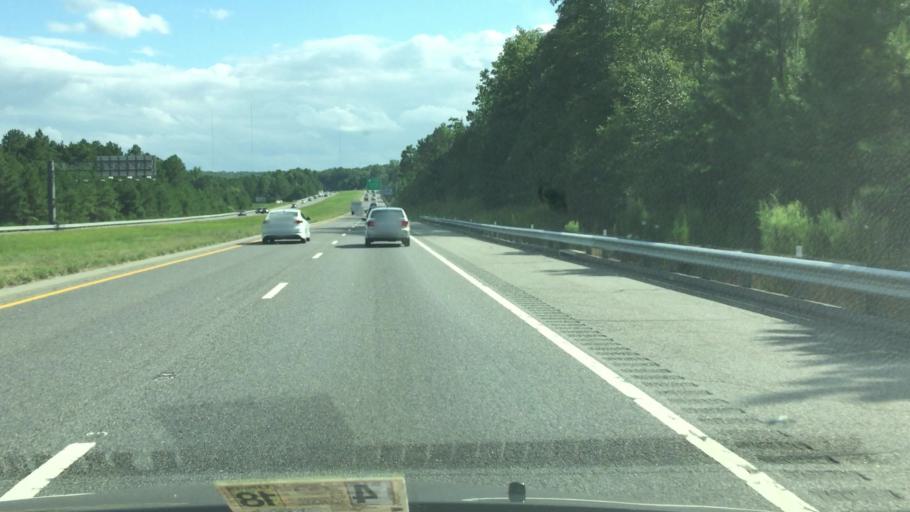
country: US
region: Virginia
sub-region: Chesterfield County
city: Brandermill
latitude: 37.5417
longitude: -77.6949
